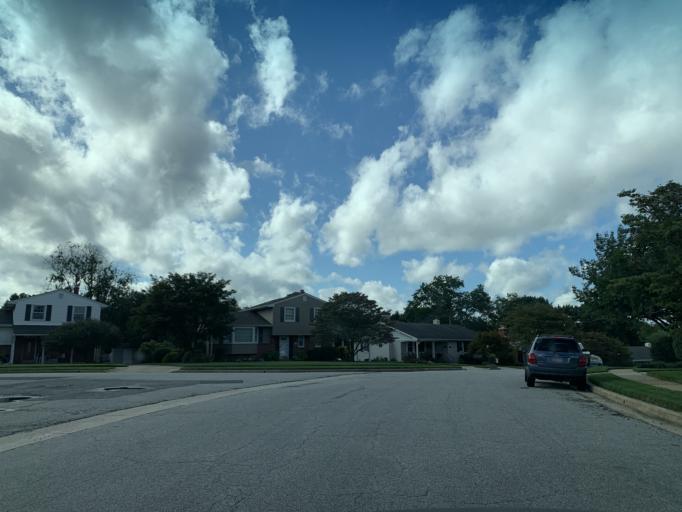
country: US
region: Maryland
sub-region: Baltimore County
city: Timonium
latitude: 39.4514
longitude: -76.6125
